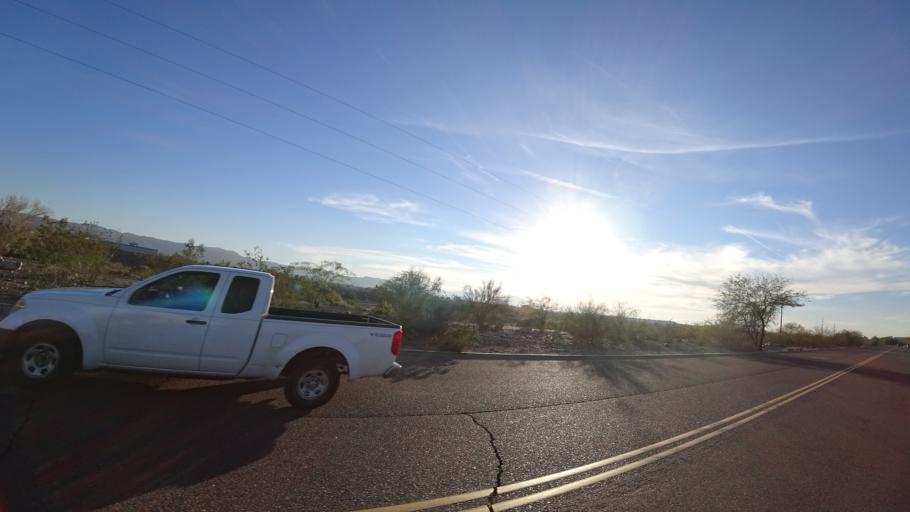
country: US
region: Arizona
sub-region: Maricopa County
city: Phoenix
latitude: 33.4203
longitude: -112.0494
